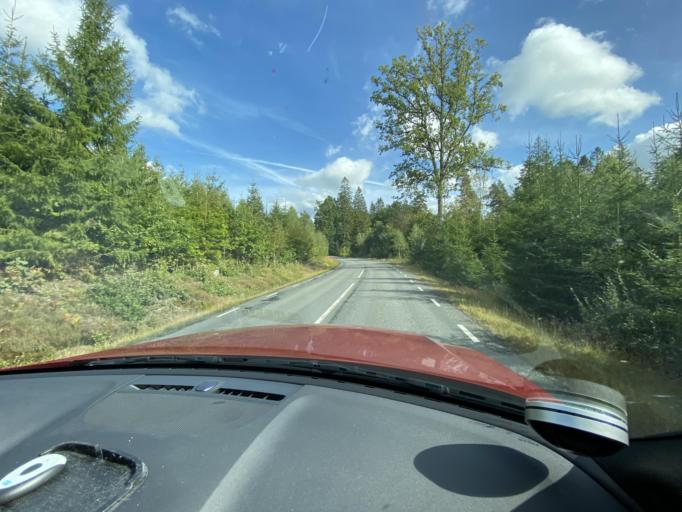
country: SE
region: Skane
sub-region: Hassleholms Kommun
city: Bjarnum
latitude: 56.3511
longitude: 13.7289
